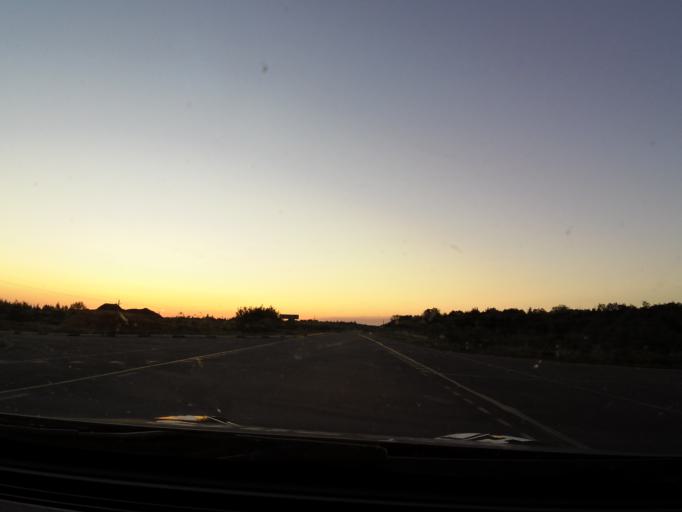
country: RU
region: Vologda
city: Vytegra
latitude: 60.9575
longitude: 36.0896
